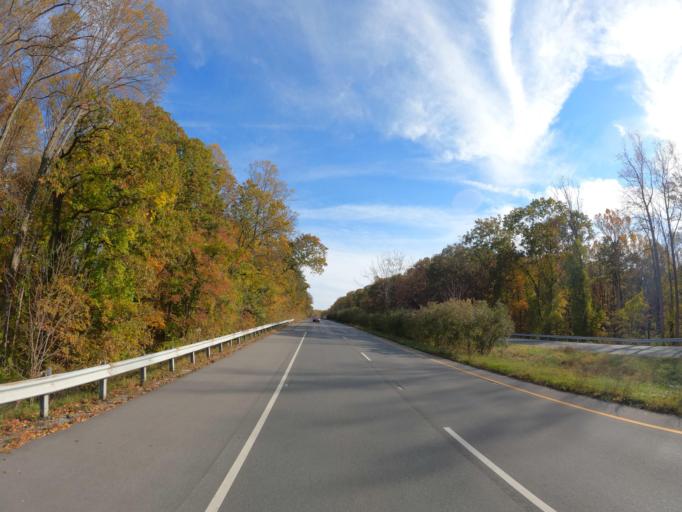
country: US
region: Maryland
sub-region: Howard County
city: Columbia
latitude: 39.3003
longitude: -76.9082
